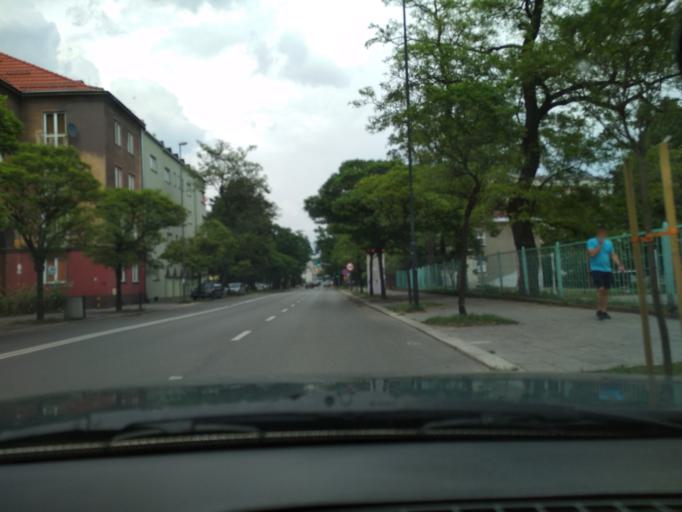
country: PL
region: Silesian Voivodeship
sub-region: Gliwice
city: Gliwice
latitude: 50.2939
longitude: 18.6775
